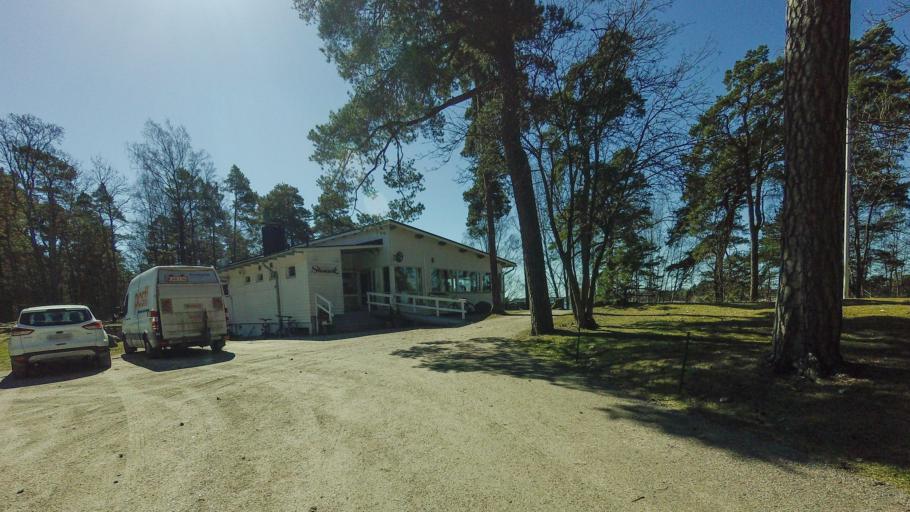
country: FI
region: Uusimaa
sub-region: Helsinki
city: Helsinki
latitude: 60.1631
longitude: 25.0293
